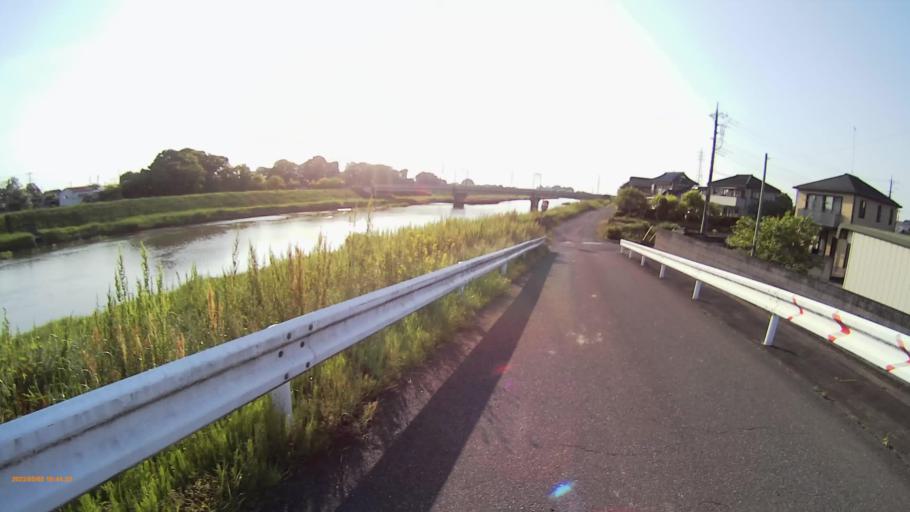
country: JP
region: Saitama
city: Satte
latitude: 36.0965
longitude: 139.7214
